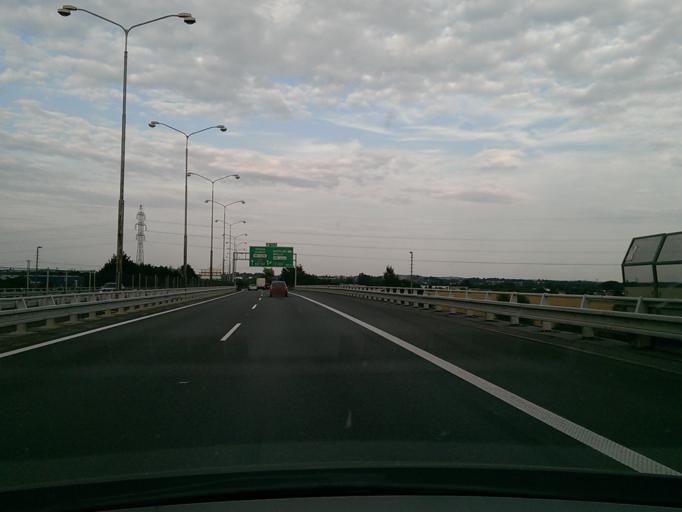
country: CZ
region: South Moravian
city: Moravany
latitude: 49.1591
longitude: 16.6065
